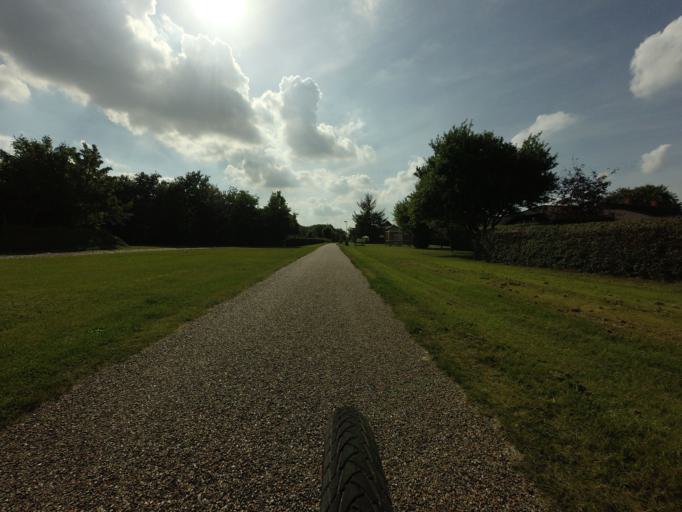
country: DK
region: Central Jutland
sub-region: Herning Kommune
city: Sunds
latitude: 56.2384
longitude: 9.0927
